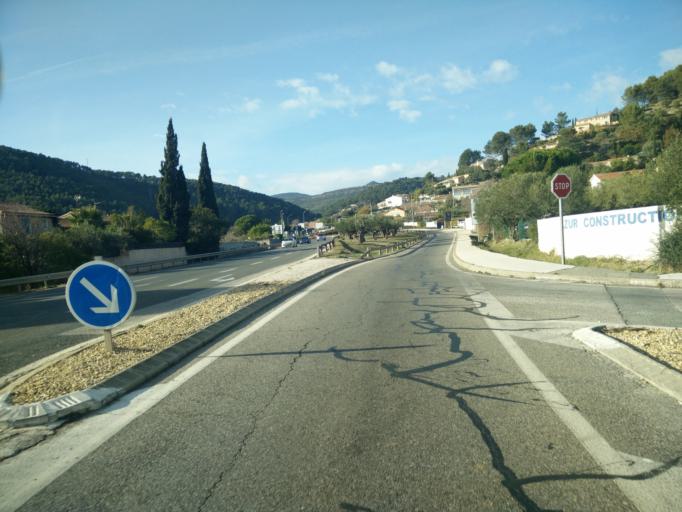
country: FR
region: Provence-Alpes-Cote d'Azur
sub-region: Departement du Var
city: Sollies-Pont
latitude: 43.1971
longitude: 6.0380
